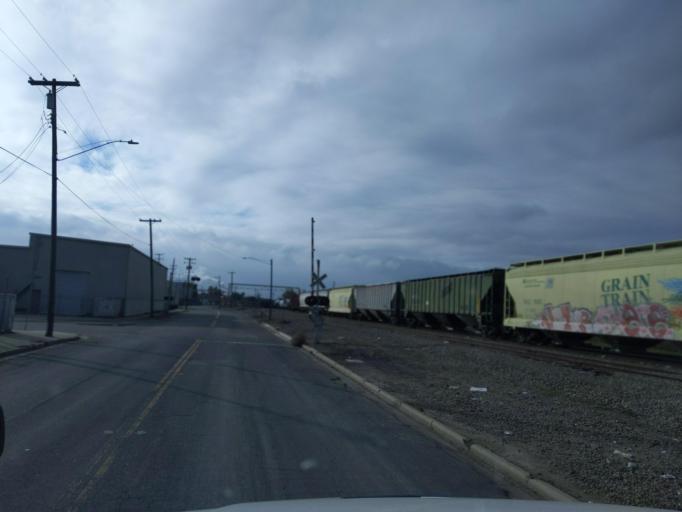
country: US
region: California
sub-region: San Joaquin County
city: Stockton
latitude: 37.9477
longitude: -121.3072
